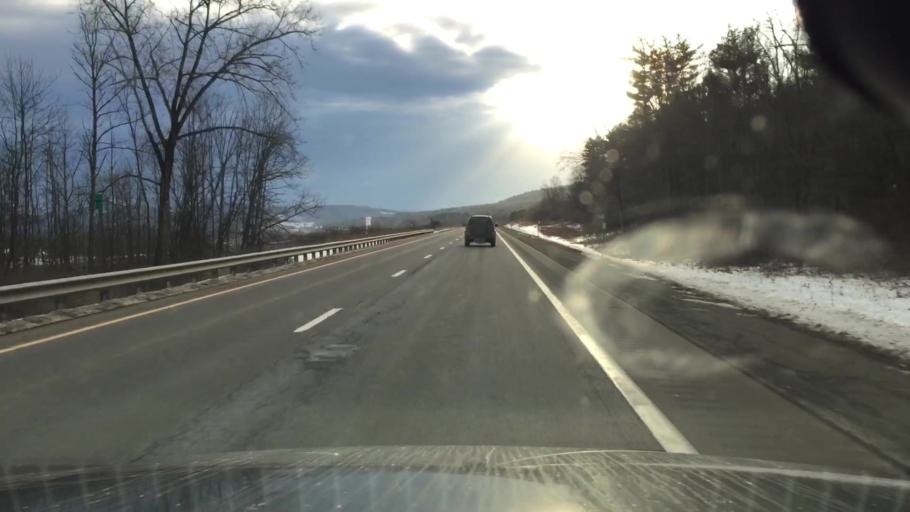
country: US
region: Pennsylvania
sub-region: Bradford County
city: Sayre
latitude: 42.0264
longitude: -76.4338
